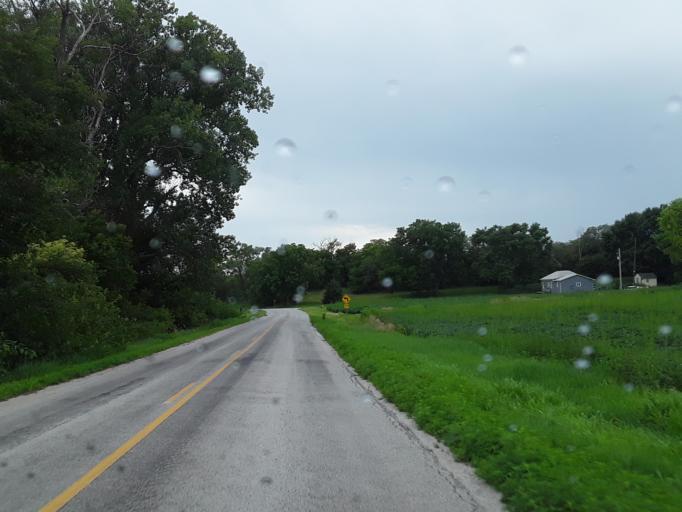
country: US
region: Nebraska
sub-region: Washington County
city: Blair
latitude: 41.5019
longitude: -96.1573
